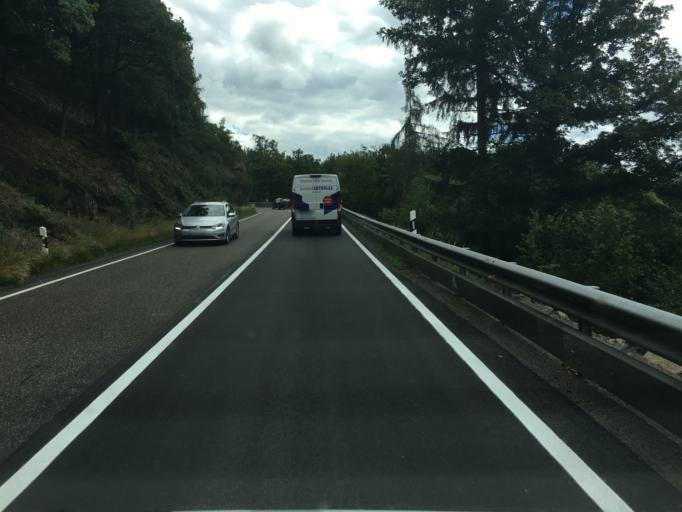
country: DE
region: North Rhine-Westphalia
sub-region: Regierungsbezirk Koln
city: Schleiden
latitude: 50.5684
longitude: 6.4158
